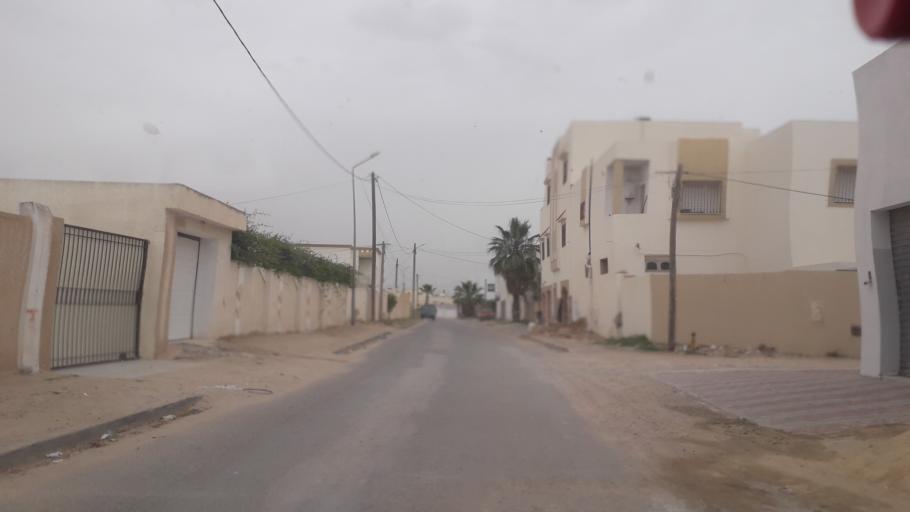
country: TN
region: Safaqis
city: Al Qarmadah
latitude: 34.7941
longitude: 10.7705
